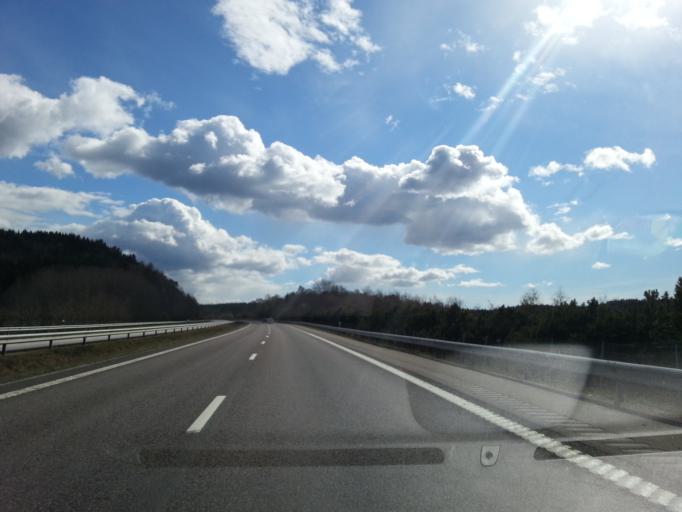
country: SE
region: Vaestra Goetaland
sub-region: Uddevalla Kommun
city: Ljungskile
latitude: 58.2009
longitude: 11.9080
